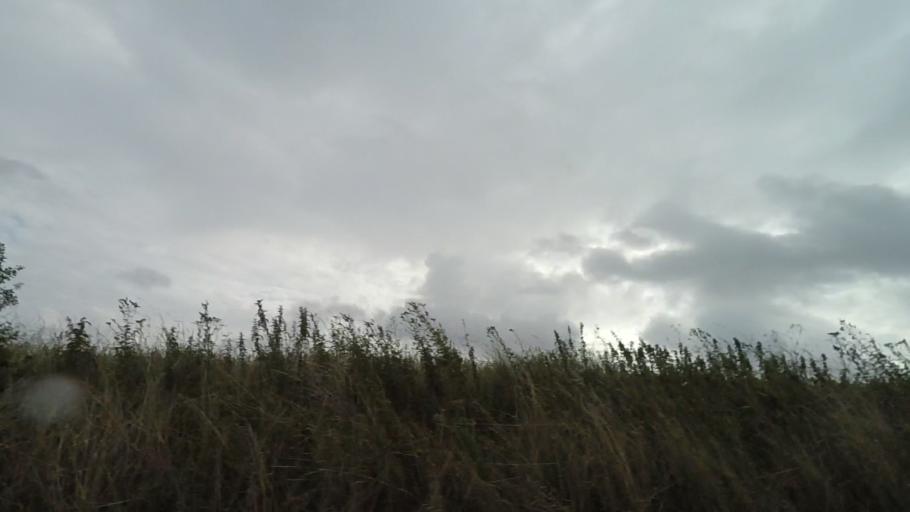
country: DK
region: Central Jutland
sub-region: Syddjurs Kommune
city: Ronde
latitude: 56.3239
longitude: 10.4587
